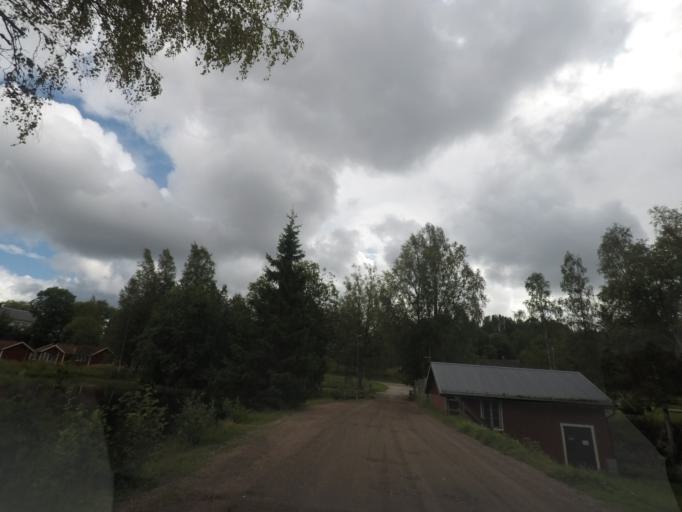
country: SE
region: Vaermland
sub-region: Filipstads Kommun
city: Lesjofors
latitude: 60.1377
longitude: 14.3923
